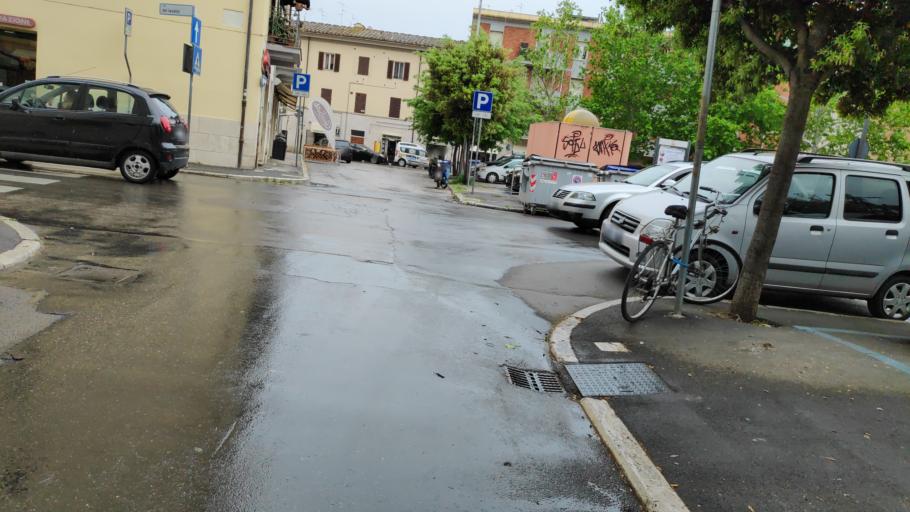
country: IT
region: Tuscany
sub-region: Provincia di Grosseto
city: Grosseto
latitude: 42.7583
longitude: 11.1155
